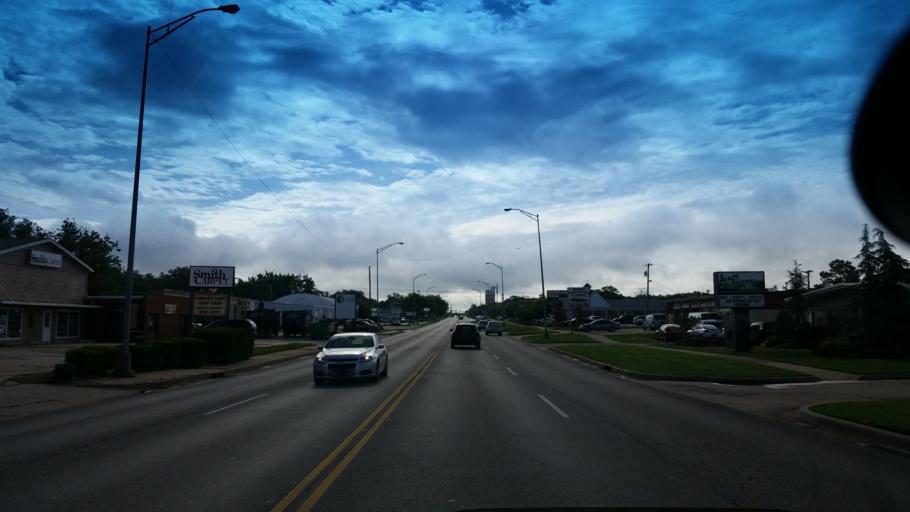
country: US
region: Oklahoma
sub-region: Oklahoma County
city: Edmond
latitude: 35.6529
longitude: -97.4945
